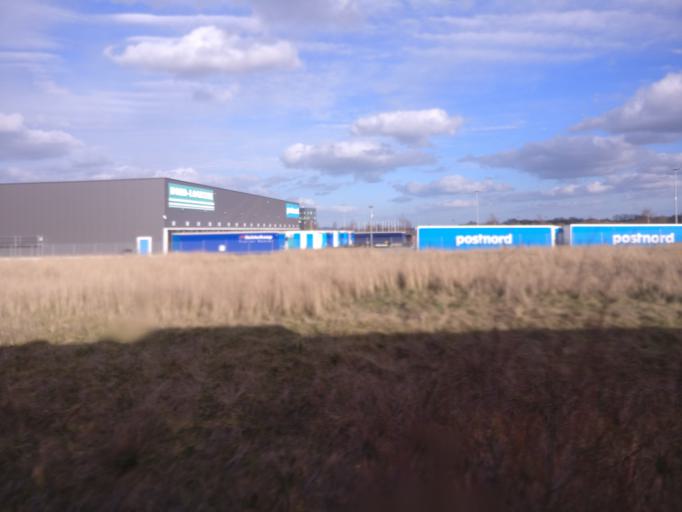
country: DE
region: Schleswig-Holstein
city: Travemuende
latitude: 53.9399
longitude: 10.8472
